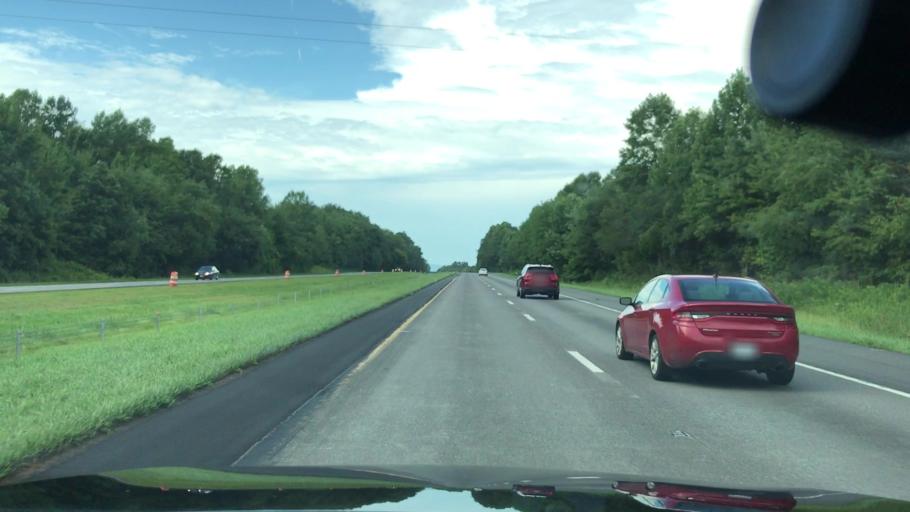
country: US
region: North Carolina
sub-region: Surry County
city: Dobson
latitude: 36.4177
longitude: -80.7785
